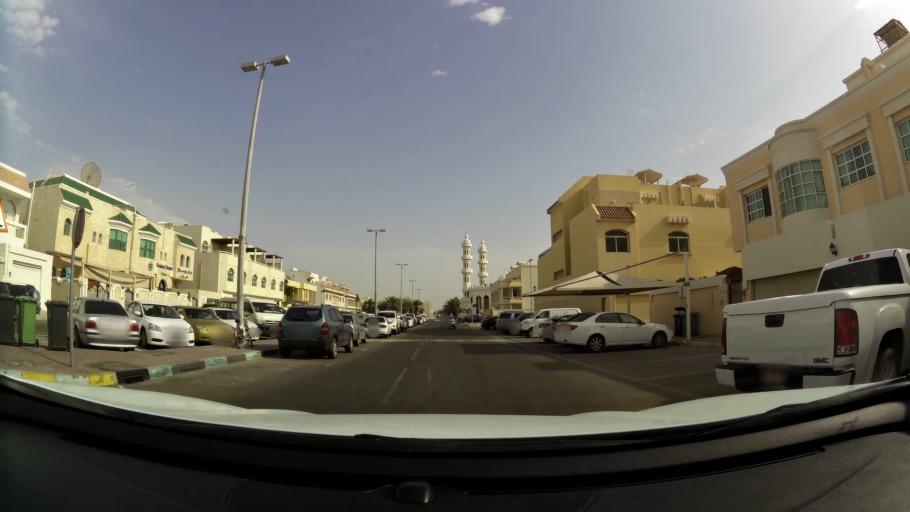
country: AE
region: Abu Dhabi
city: Abu Dhabi
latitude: 24.4676
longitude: 54.3523
